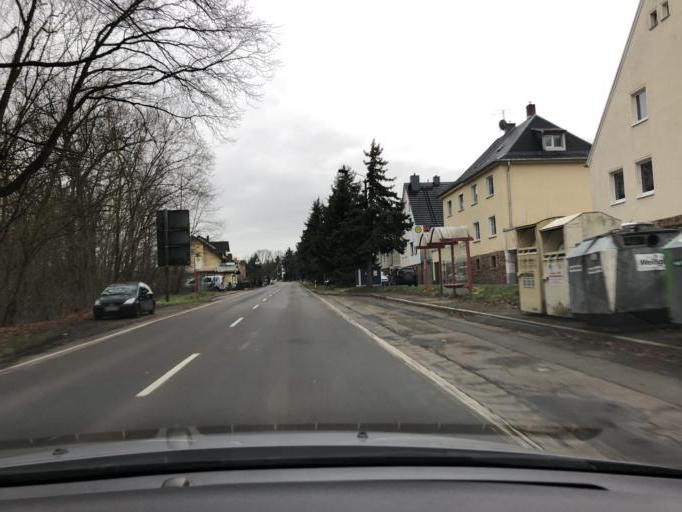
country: DE
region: Saxony
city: Ebersbach
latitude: 51.1044
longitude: 13.1309
